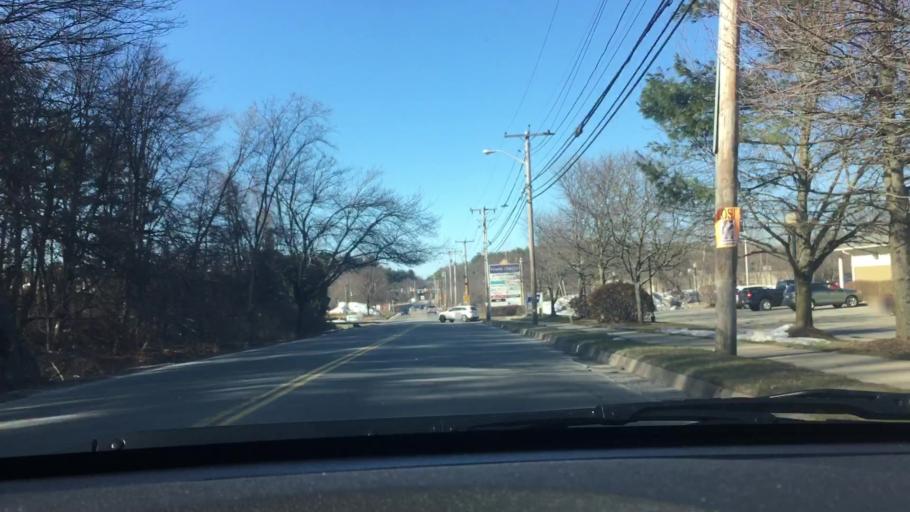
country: US
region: Massachusetts
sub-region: Worcester County
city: Cordaville
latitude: 42.2864
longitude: -71.5259
